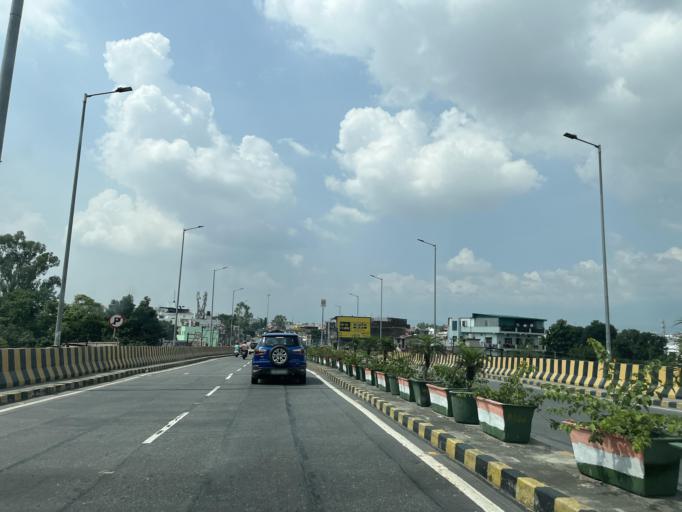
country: IN
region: Uttarakhand
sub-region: Dehradun
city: Raipur
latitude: 30.2779
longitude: 78.0739
